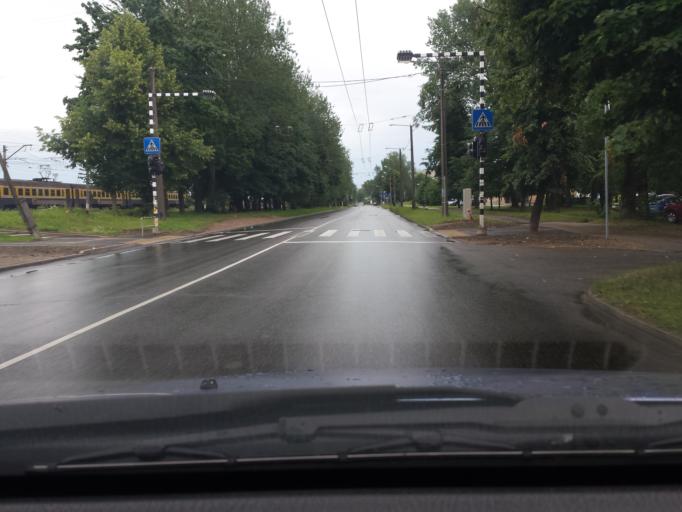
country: LV
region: Kekava
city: Balozi
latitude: 56.9190
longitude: 24.1851
